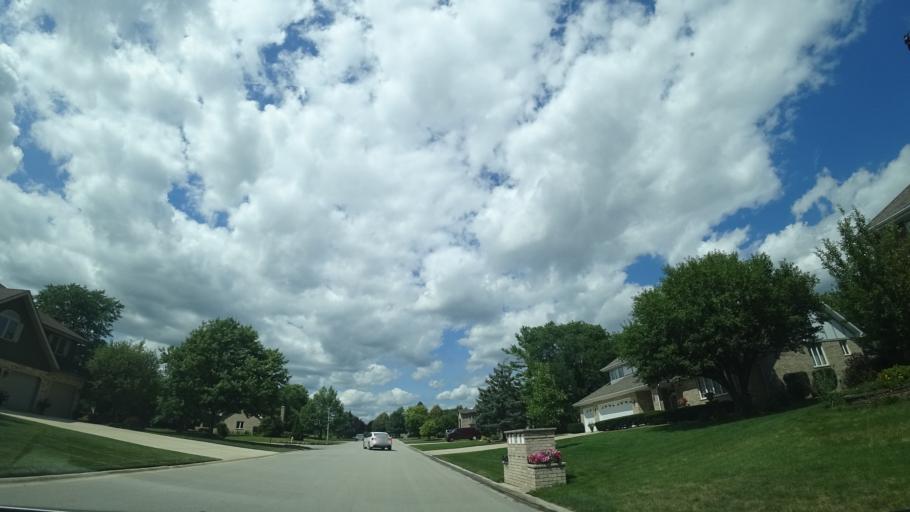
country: US
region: Illinois
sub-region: Will County
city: Homer Glen
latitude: 41.5832
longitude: -87.9110
